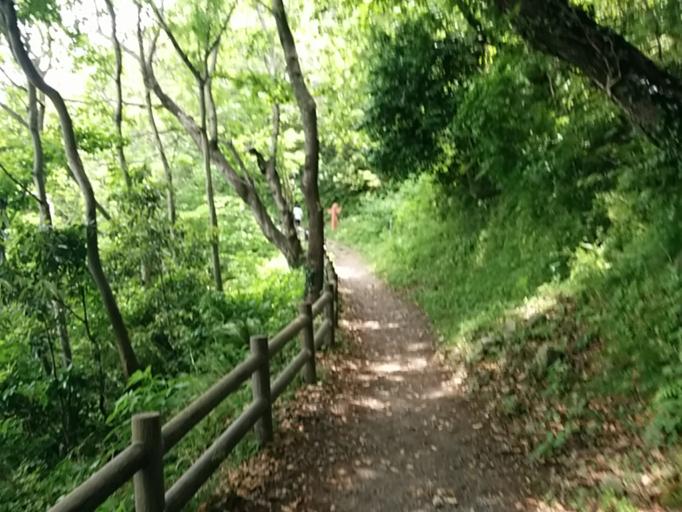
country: JP
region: Kyoto
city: Miyazu
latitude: 35.7763
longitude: 135.2233
